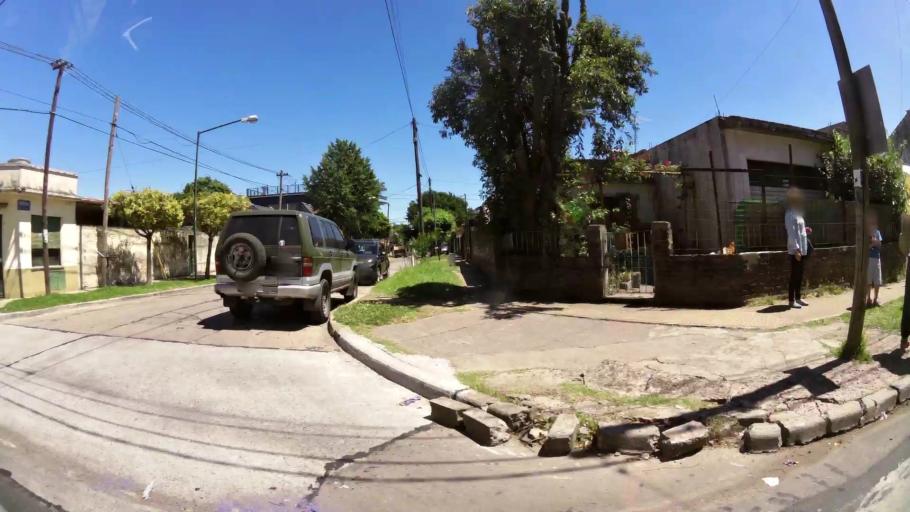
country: AR
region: Buenos Aires
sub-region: Partido de San Isidro
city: San Isidro
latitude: -34.5059
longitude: -58.5514
